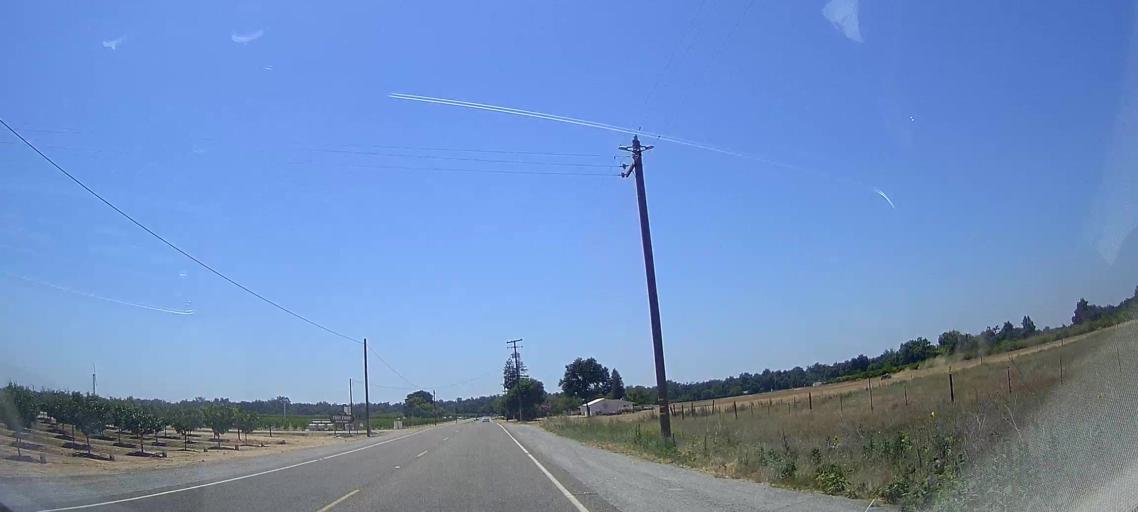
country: US
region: California
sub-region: Fresno County
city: Minkler
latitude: 36.7193
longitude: -119.4524
